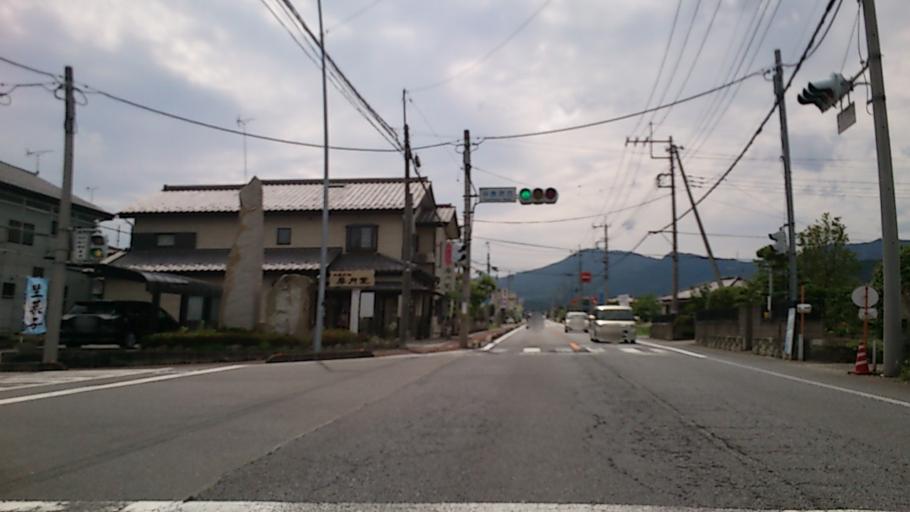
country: JP
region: Gunma
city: Tomioka
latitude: 36.2416
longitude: 138.8418
